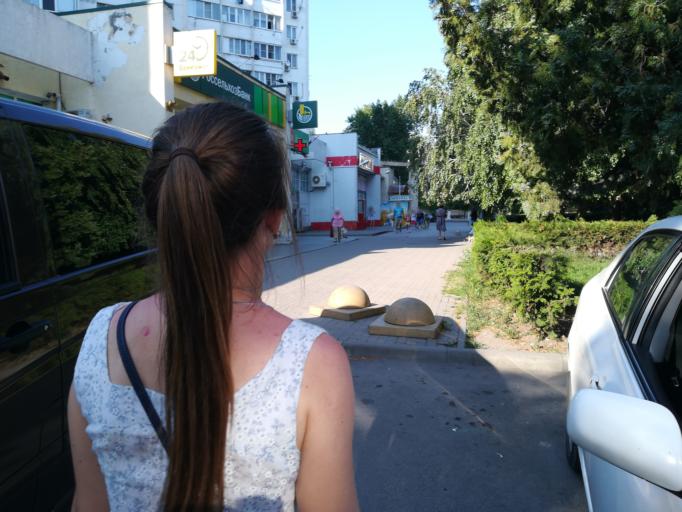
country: RU
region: Krasnodarskiy
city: Anapa
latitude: 44.9009
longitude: 37.3313
